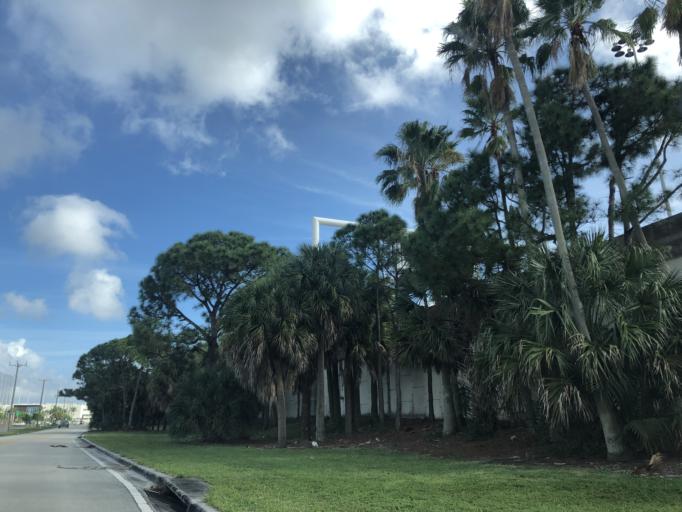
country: US
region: Florida
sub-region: Palm Beach County
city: Haverhill
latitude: 26.6899
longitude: -80.0827
